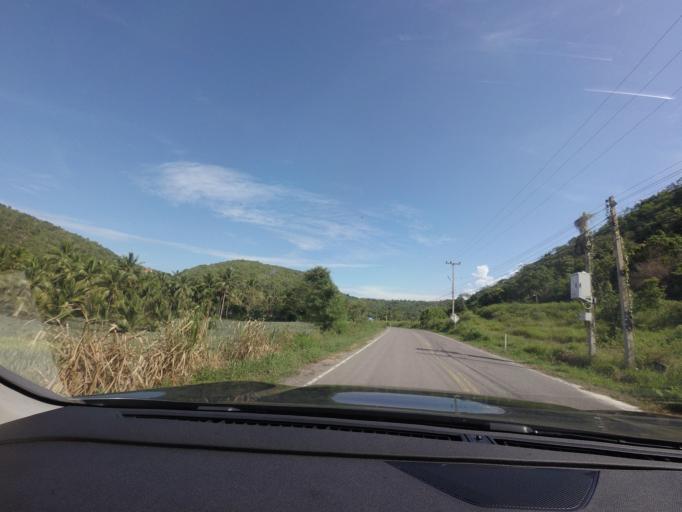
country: TH
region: Prachuap Khiri Khan
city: Pran Buri
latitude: 12.4648
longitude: 99.9456
